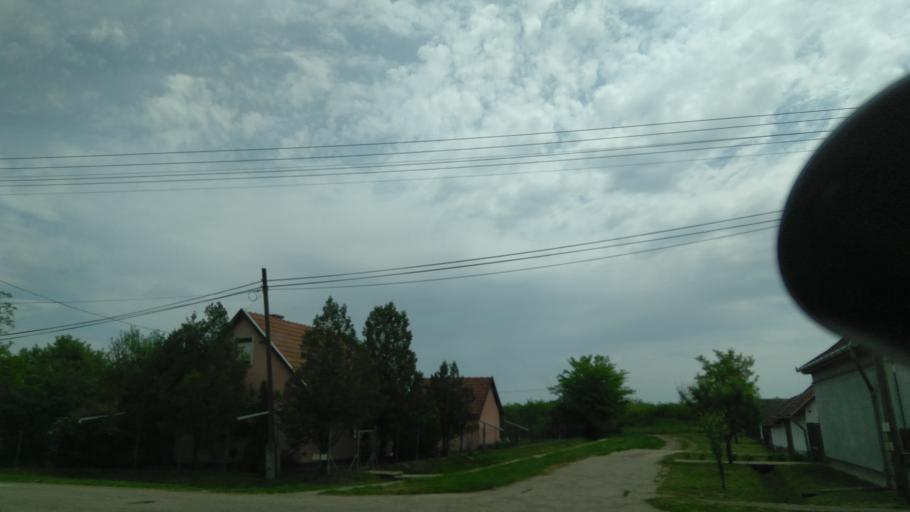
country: HU
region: Bekes
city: Fuzesgyarmat
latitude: 47.0990
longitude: 21.2127
